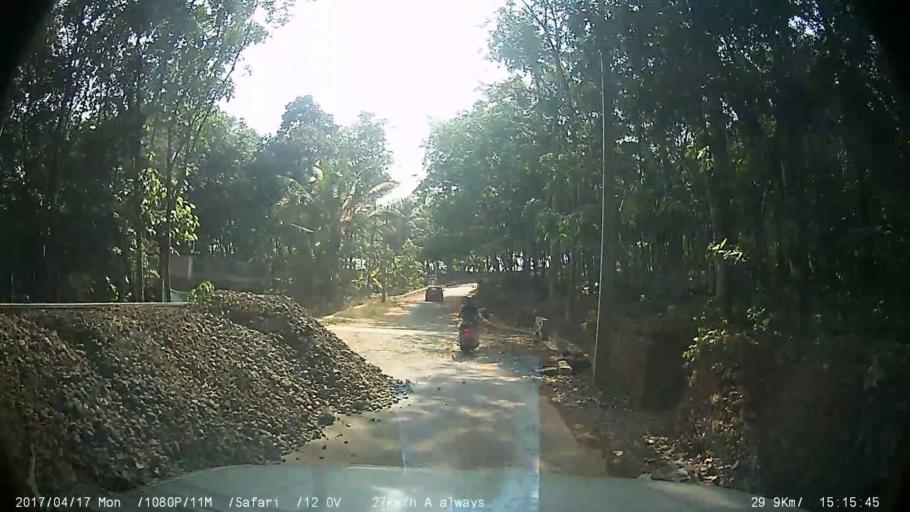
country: IN
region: Kerala
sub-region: Ernakulam
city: Ramamangalam
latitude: 9.9034
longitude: 76.4712
